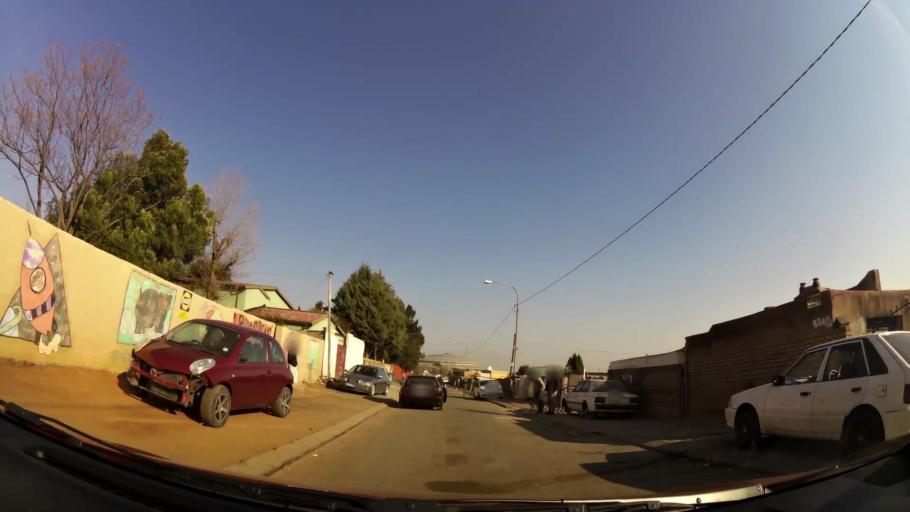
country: ZA
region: Gauteng
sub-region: City of Johannesburg Metropolitan Municipality
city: Soweto
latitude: -26.2574
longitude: 27.9472
